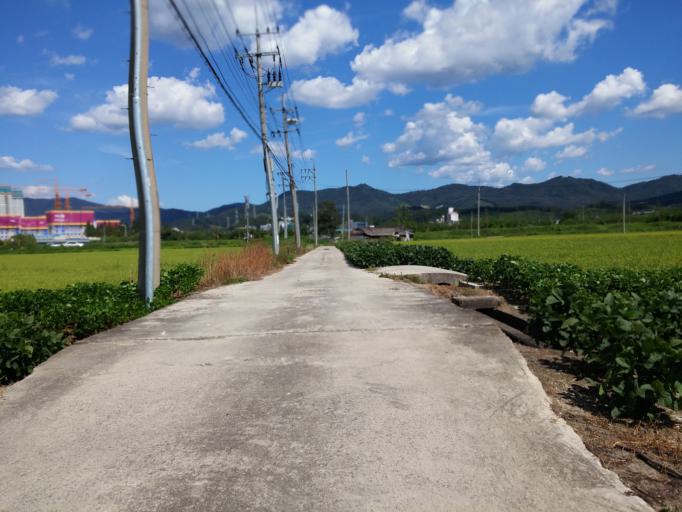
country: KR
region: Chungcheongbuk-do
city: Cheongju-si
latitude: 36.5947
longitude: 127.4952
